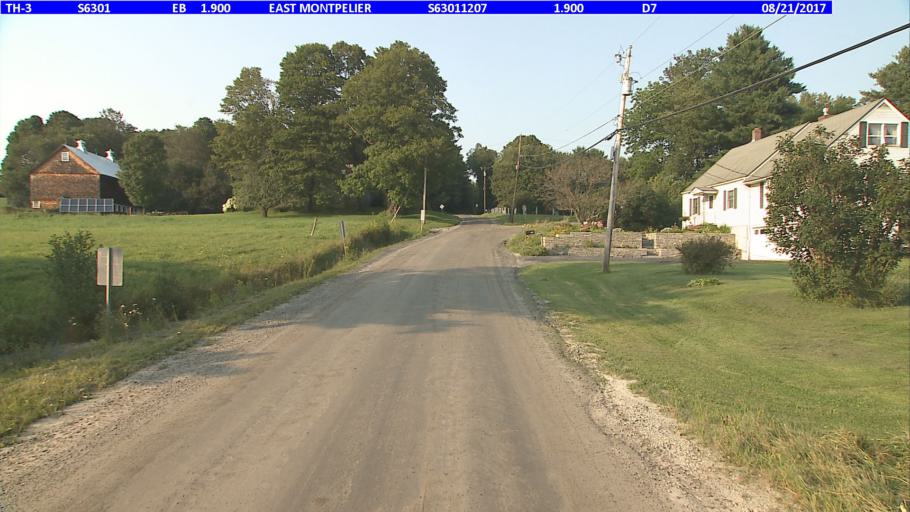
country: US
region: Vermont
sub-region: Washington County
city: Montpelier
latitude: 44.2861
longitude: -72.5217
